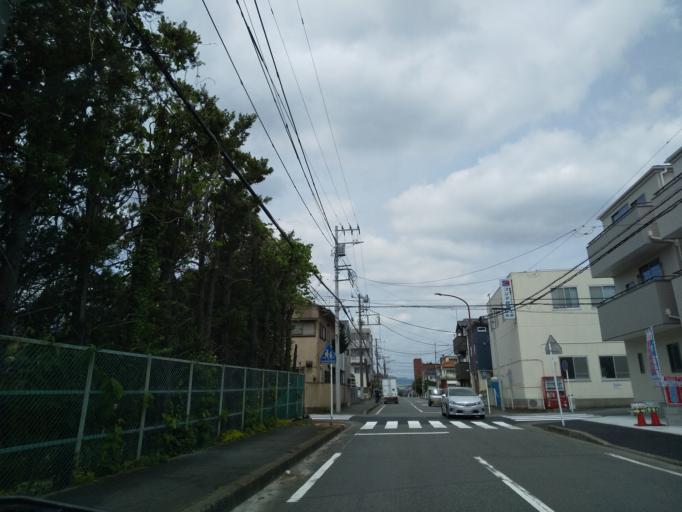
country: JP
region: Kanagawa
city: Zama
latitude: 35.5697
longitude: 139.3654
